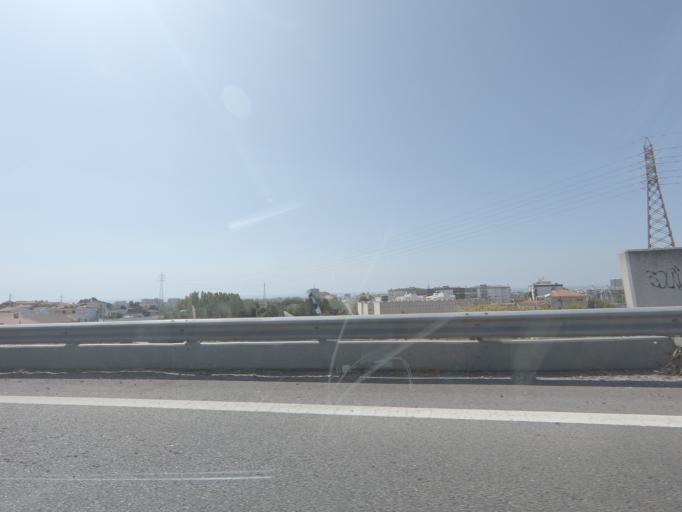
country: PT
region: Porto
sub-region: Matosinhos
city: Guifoes
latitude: 41.1885
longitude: -8.6704
